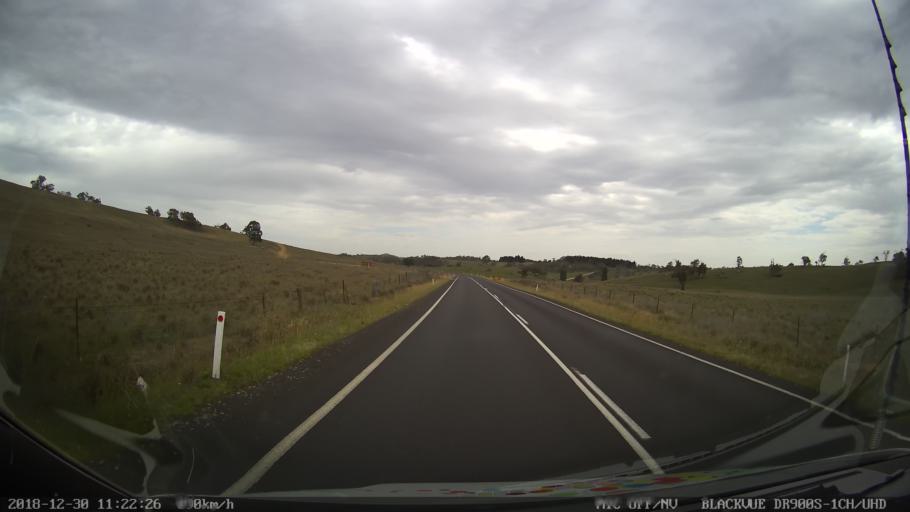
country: AU
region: New South Wales
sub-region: Snowy River
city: Jindabyne
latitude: -36.4998
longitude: 148.6712
